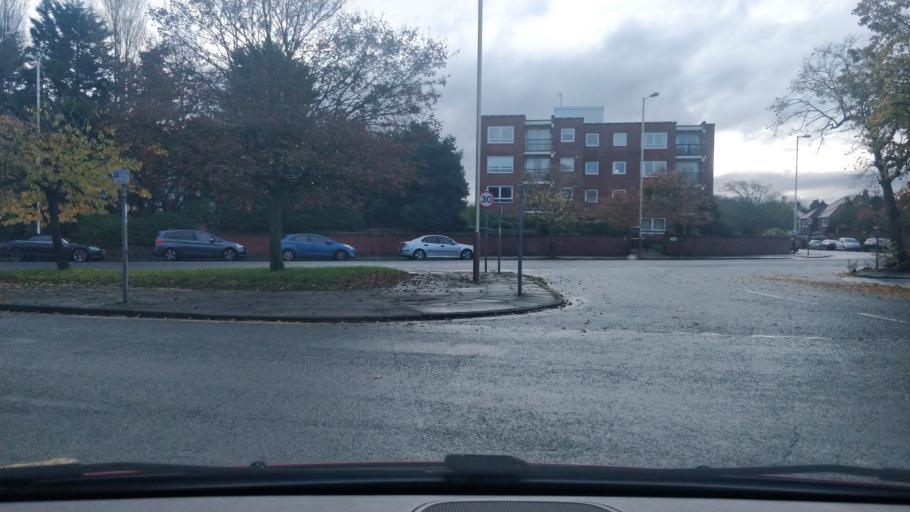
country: GB
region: England
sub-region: Sefton
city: Southport
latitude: 53.6425
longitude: -3.0163
